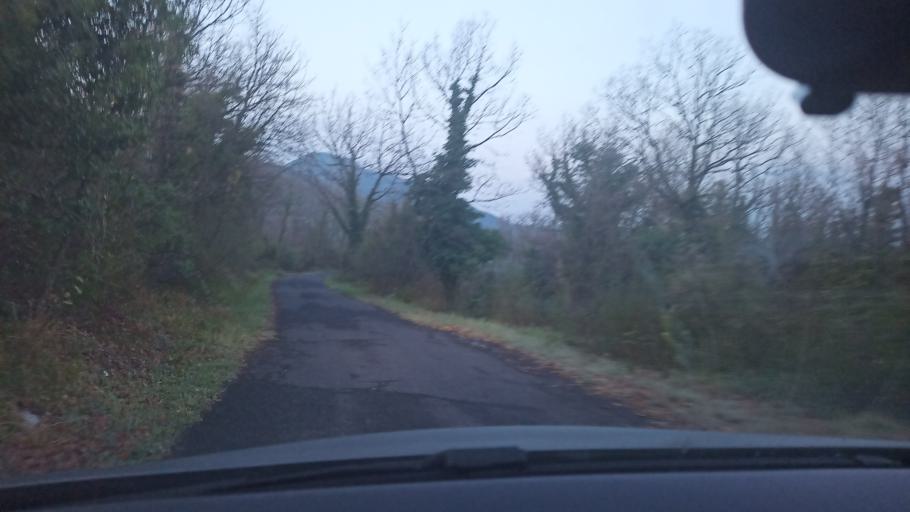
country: IT
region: Latium
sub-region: Provincia di Rieti
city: Cottanello
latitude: 42.4052
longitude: 12.6812
